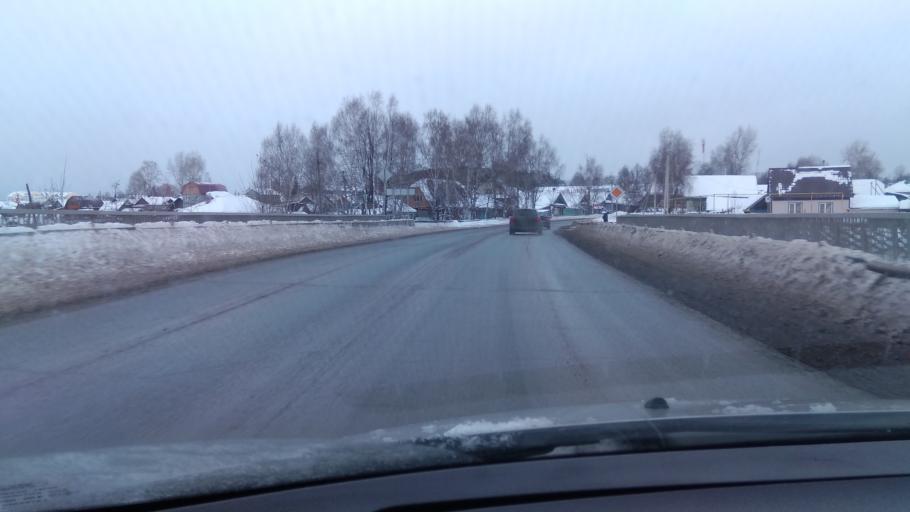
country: RU
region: Sverdlovsk
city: Nikolo-Pavlovskoye
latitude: 57.7853
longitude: 60.0562
